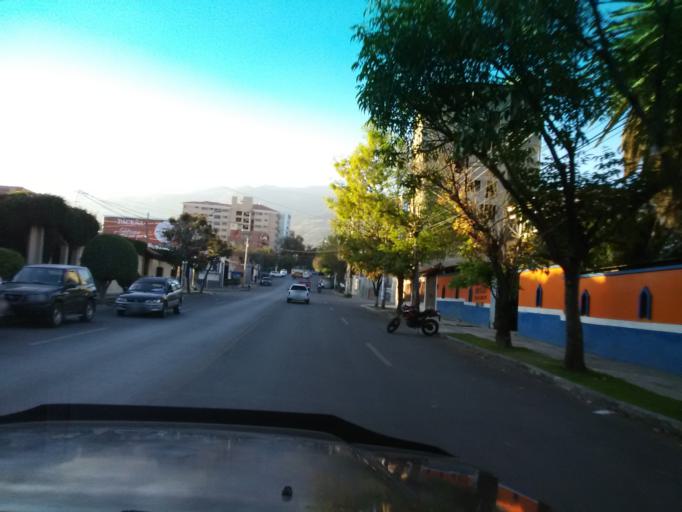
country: BO
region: Cochabamba
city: Cochabamba
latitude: -17.3714
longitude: -66.1568
